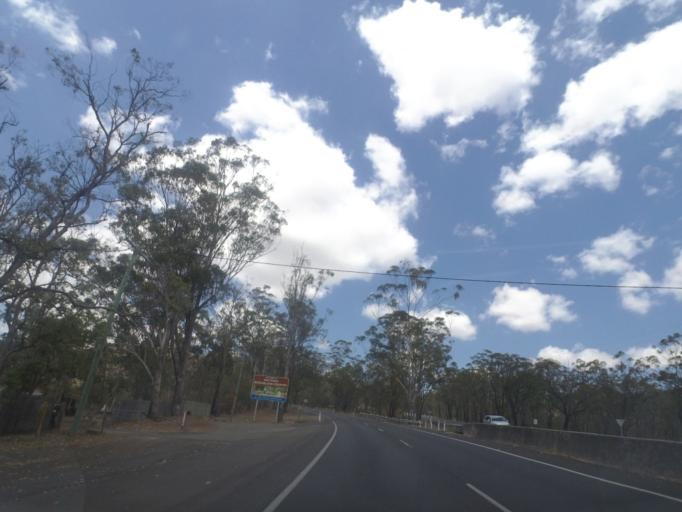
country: AU
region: Queensland
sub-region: Toowoomba
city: East Toowoomba
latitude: -27.5649
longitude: 151.9999
